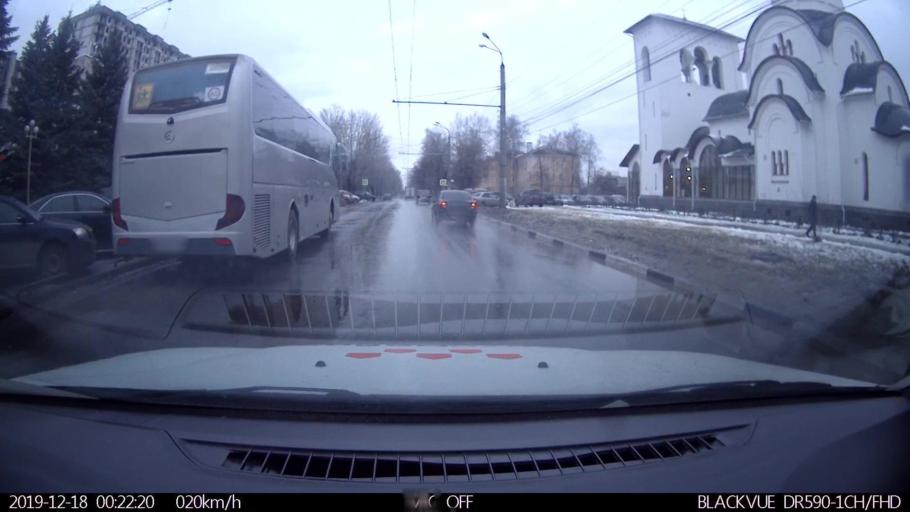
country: RU
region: Nizjnij Novgorod
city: Nizhniy Novgorod
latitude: 56.3310
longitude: 43.8844
